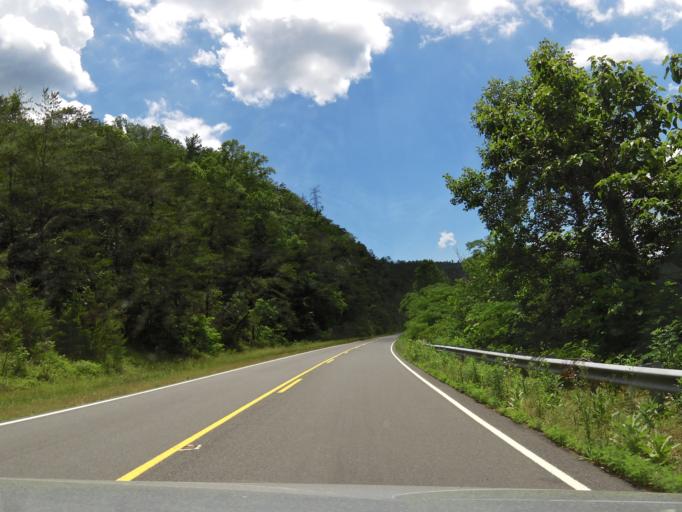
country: US
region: Tennessee
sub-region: Blount County
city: Maryville
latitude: 35.5540
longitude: -83.9955
